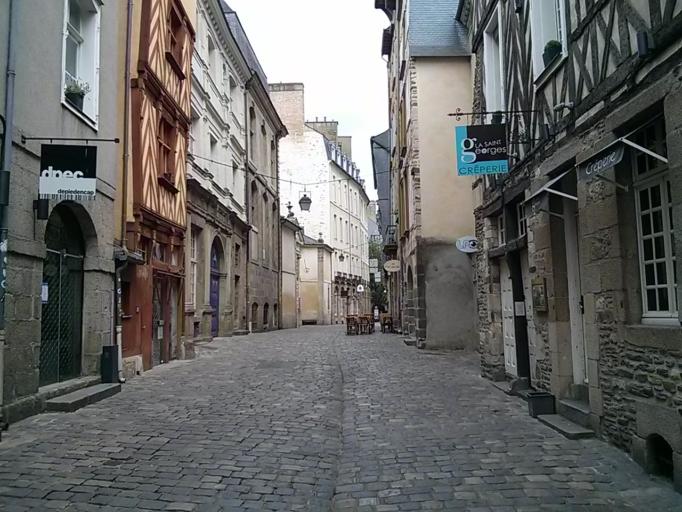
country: FR
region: Brittany
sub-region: Departement d'Ille-et-Vilaine
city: Rennes
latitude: 48.1111
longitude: -1.6825
